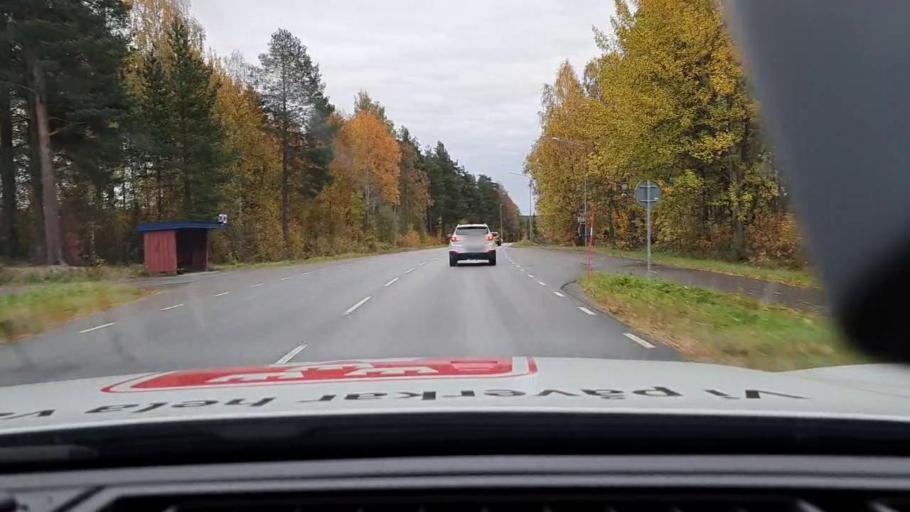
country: SE
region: Norrbotten
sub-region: Bodens Kommun
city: Saevast
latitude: 65.7698
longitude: 21.7332
